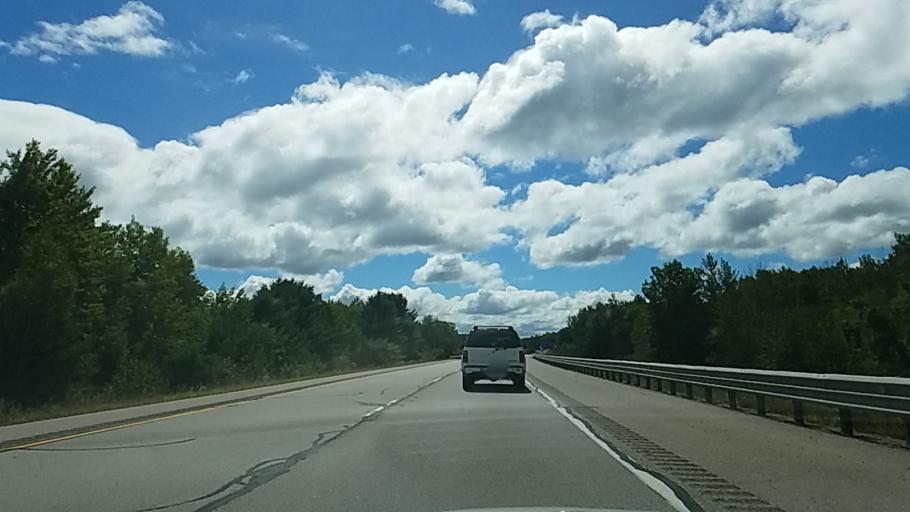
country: US
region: Michigan
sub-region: Ogemaw County
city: Skidway Lake
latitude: 44.1189
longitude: -84.1215
